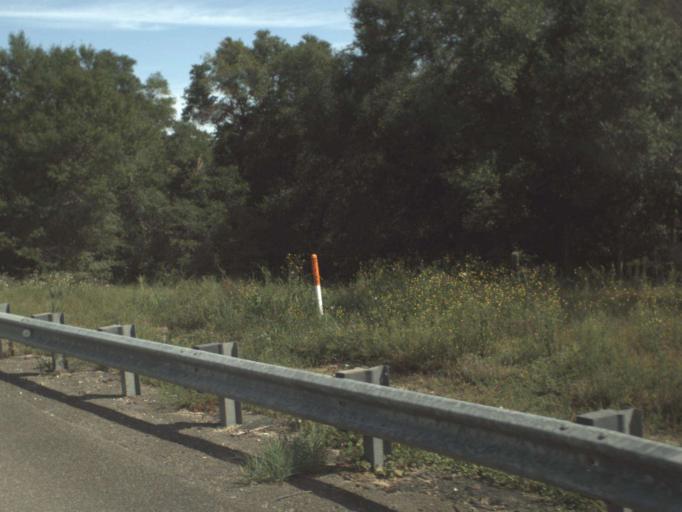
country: US
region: Florida
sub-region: Bay County
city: Lynn Haven
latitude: 30.4478
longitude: -85.6883
